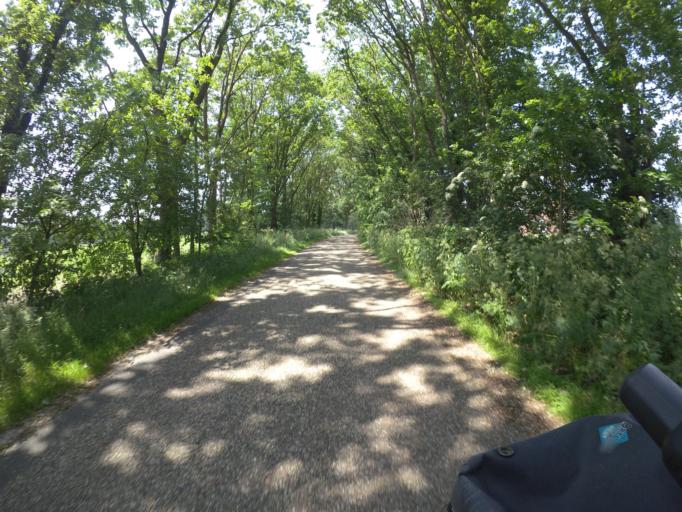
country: NL
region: Overijssel
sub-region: Gemeente Hof van Twente
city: Markelo
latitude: 52.2736
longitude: 6.4715
